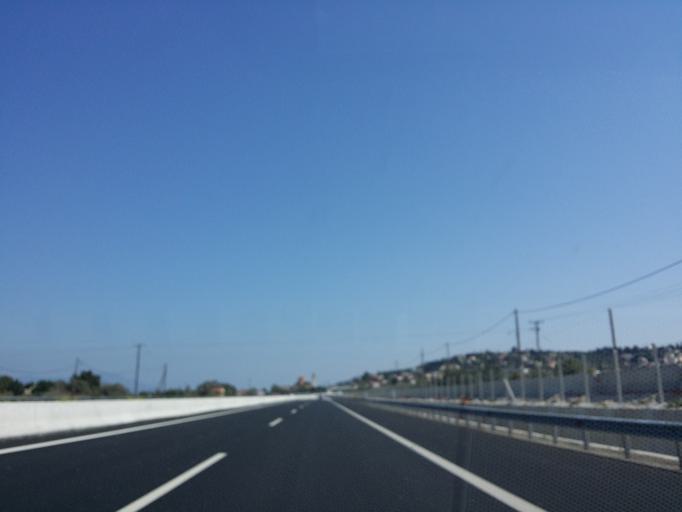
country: GR
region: Peloponnese
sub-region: Nomos Korinthias
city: Xylokastro
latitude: 38.0544
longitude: 22.6746
